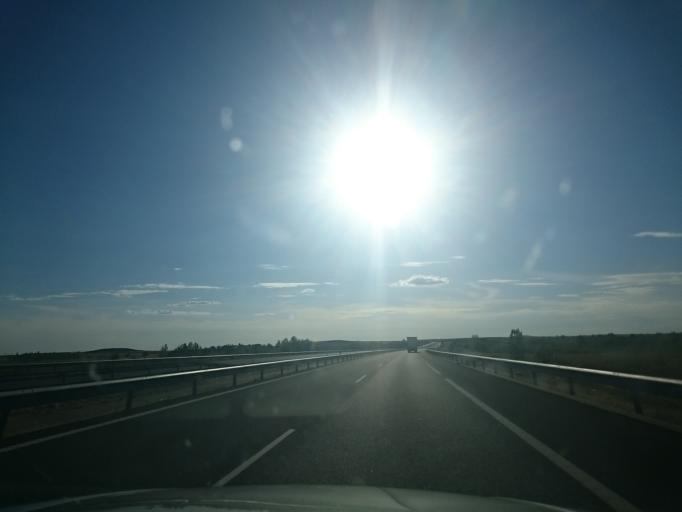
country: ES
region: Castille and Leon
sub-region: Provincia de Burgos
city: Villasandino
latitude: 42.3942
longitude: -4.1033
